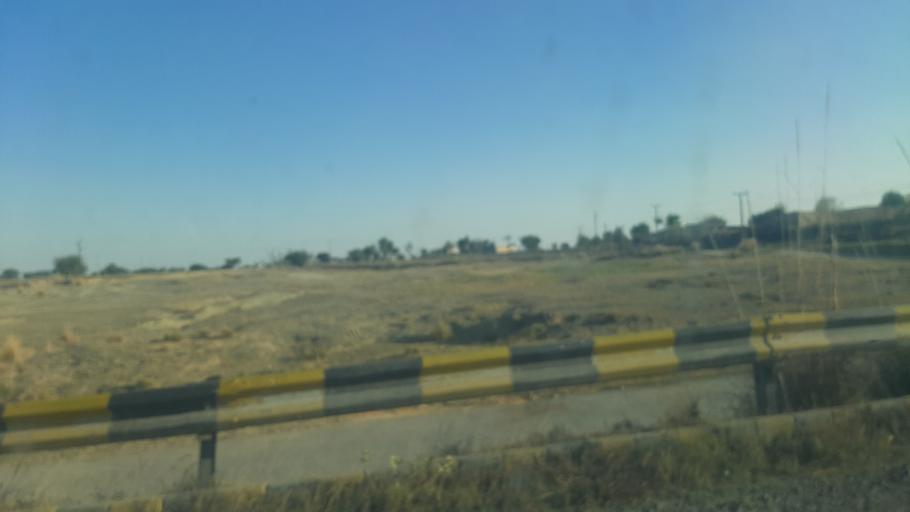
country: PK
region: Punjab
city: Talagang
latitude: 32.8893
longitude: 72.2219
